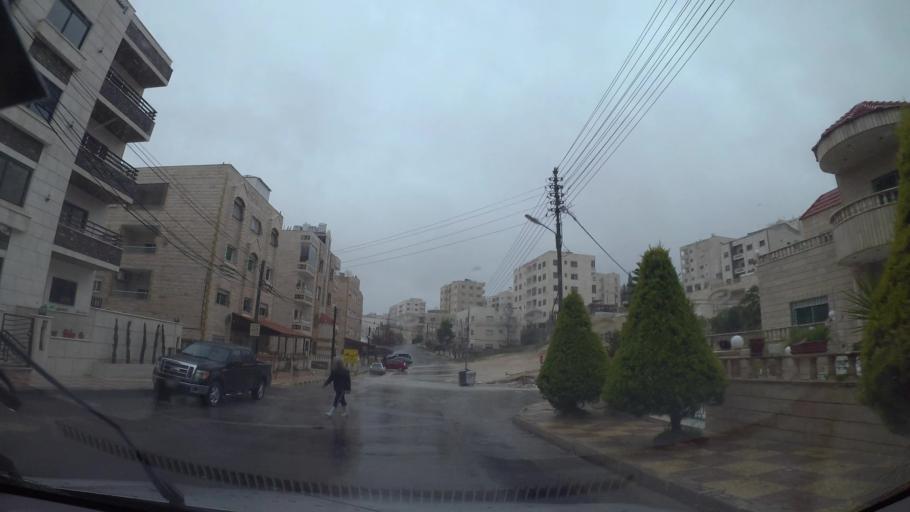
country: JO
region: Amman
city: Al Jubayhah
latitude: 32.0202
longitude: 35.8940
